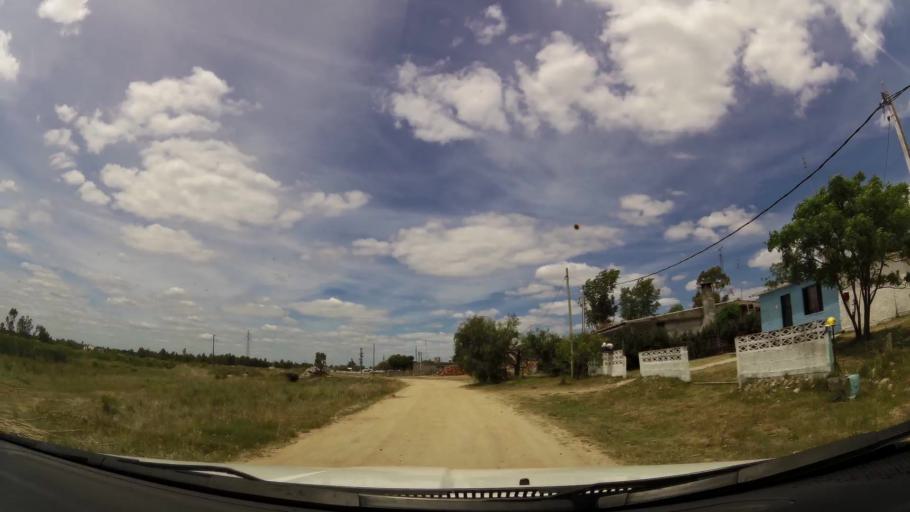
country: UY
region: San Jose
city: Delta del Tigre
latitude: -34.7704
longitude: -56.3775
